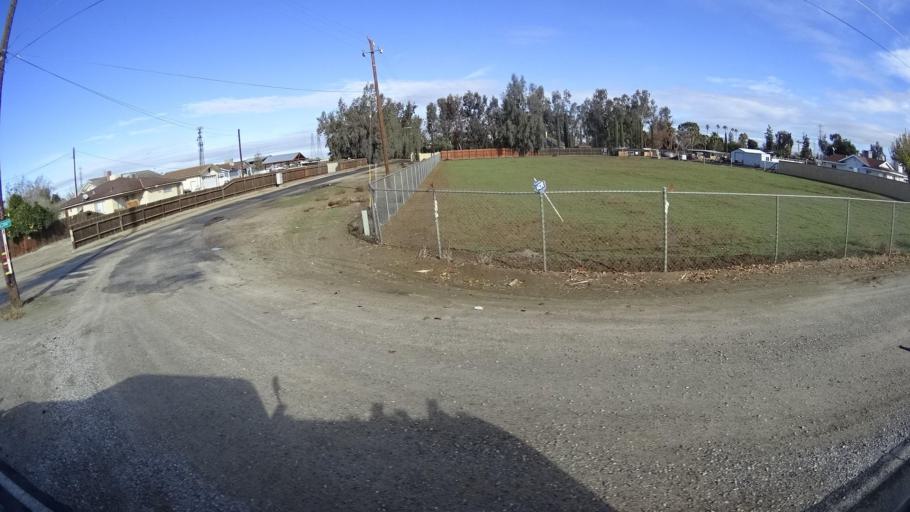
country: US
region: California
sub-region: Kern County
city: Rosedale
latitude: 35.3835
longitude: -119.1940
